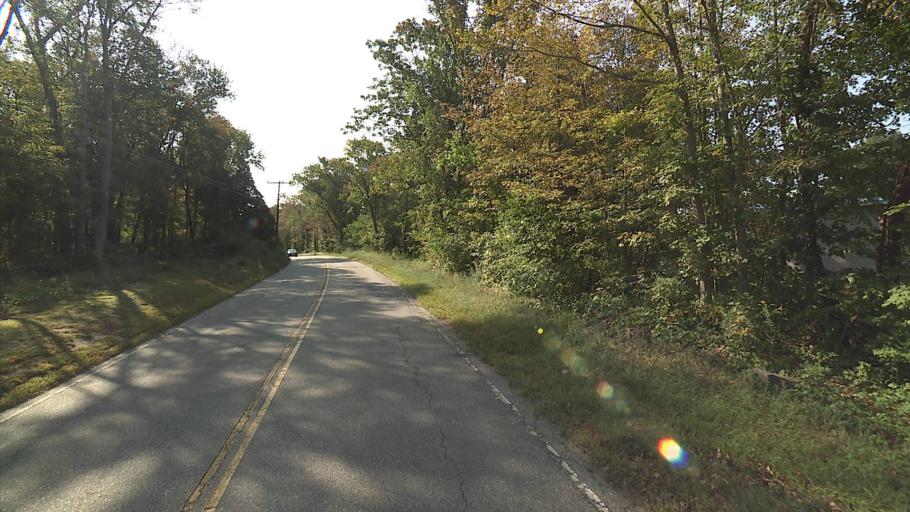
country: US
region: Connecticut
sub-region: Windham County
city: Willimantic
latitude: 41.6536
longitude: -72.2459
